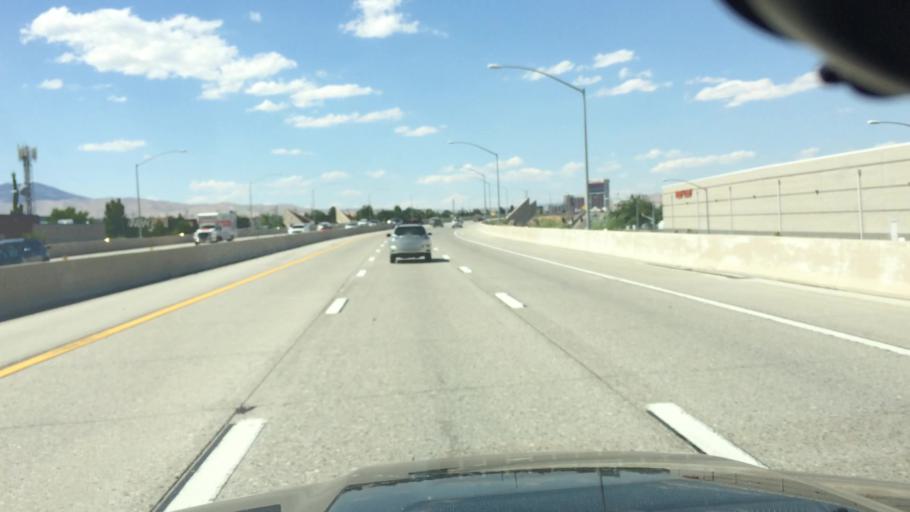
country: US
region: Nevada
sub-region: Washoe County
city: Reno
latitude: 39.4721
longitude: -119.7902
